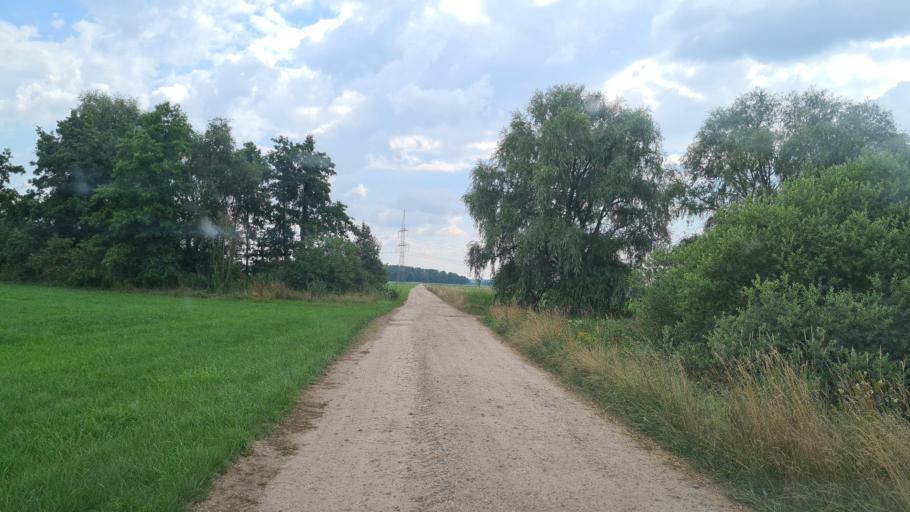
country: DE
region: Brandenburg
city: Sallgast
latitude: 51.6336
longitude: 13.8675
